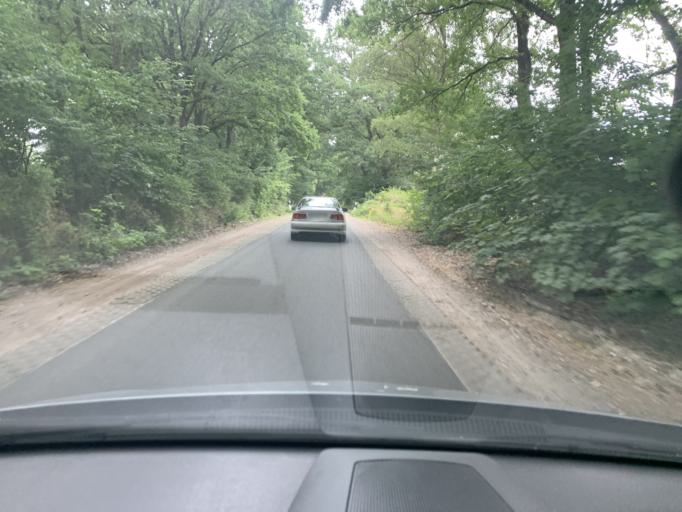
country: DE
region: Schleswig-Holstein
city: Grambek
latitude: 53.5655
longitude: 10.6863
